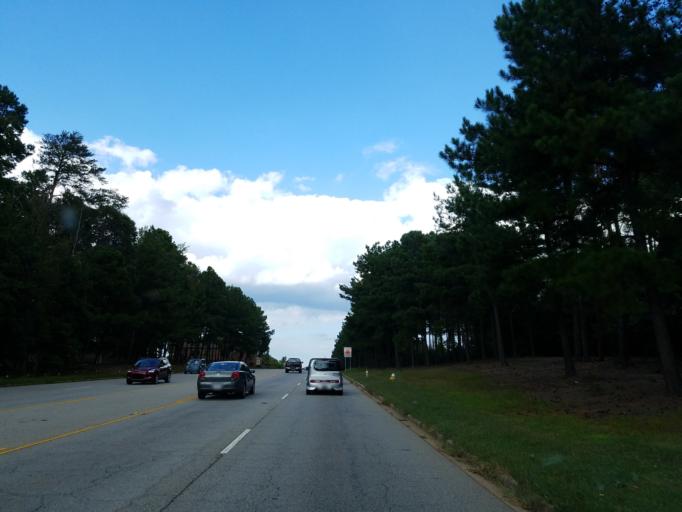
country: US
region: South Carolina
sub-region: Greenville County
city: Mauldin
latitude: 34.8223
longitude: -82.3314
